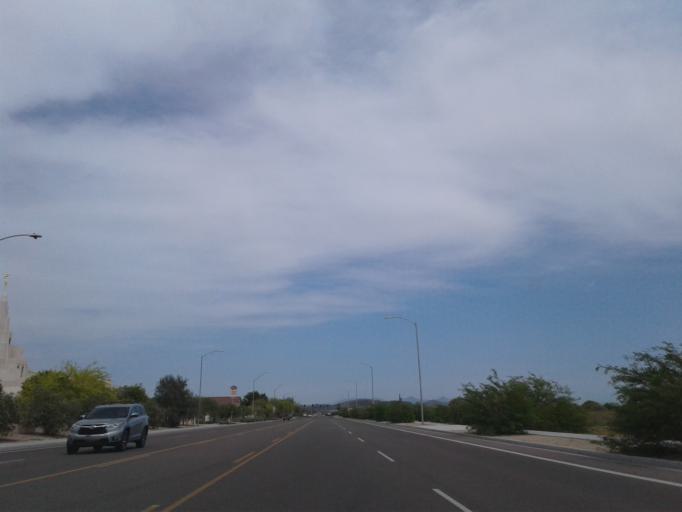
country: US
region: Arizona
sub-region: Maricopa County
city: Peoria
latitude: 33.6979
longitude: -112.1741
